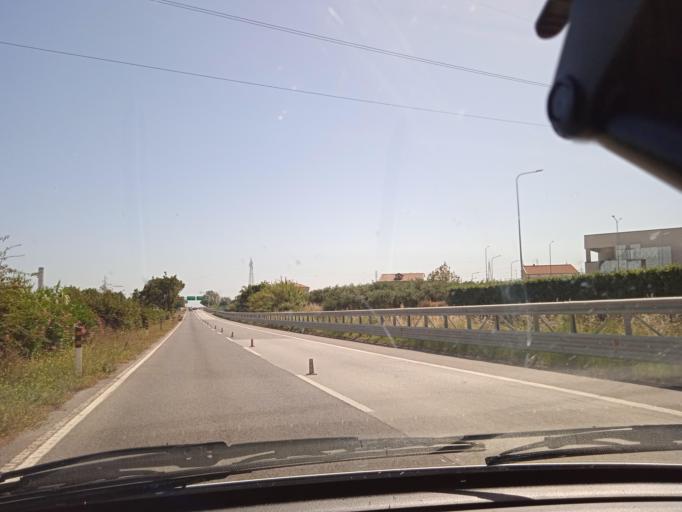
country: IT
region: Sicily
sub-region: Messina
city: San Filippo del Mela
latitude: 38.1886
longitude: 15.2672
